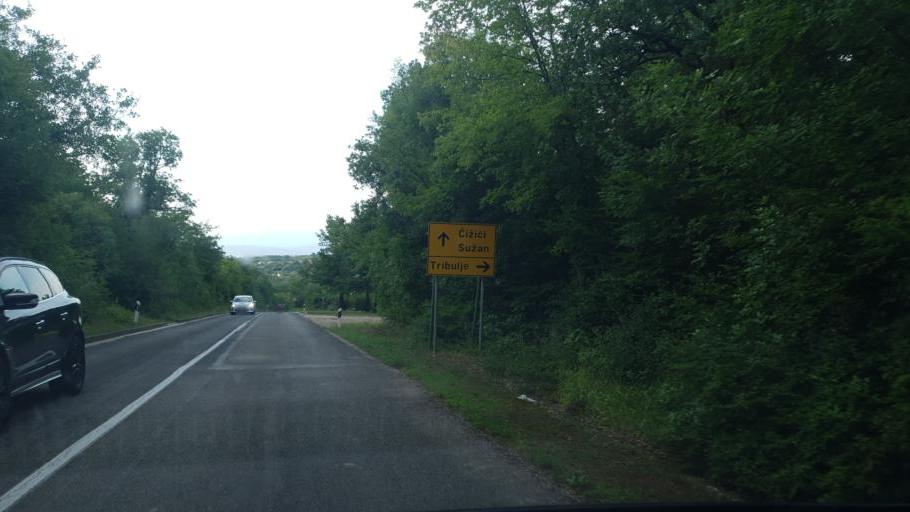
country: HR
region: Primorsko-Goranska
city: Njivice
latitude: 45.1360
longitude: 14.5838
